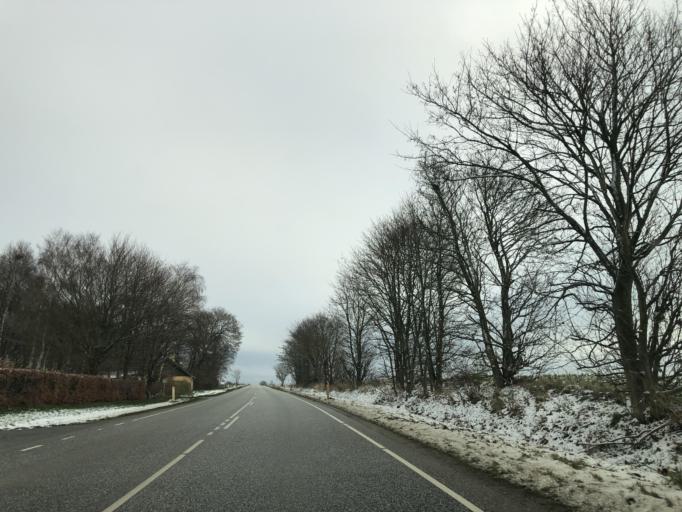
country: DK
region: Central Jutland
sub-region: Horsens Kommune
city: Braedstrup
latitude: 55.8922
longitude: 9.6649
